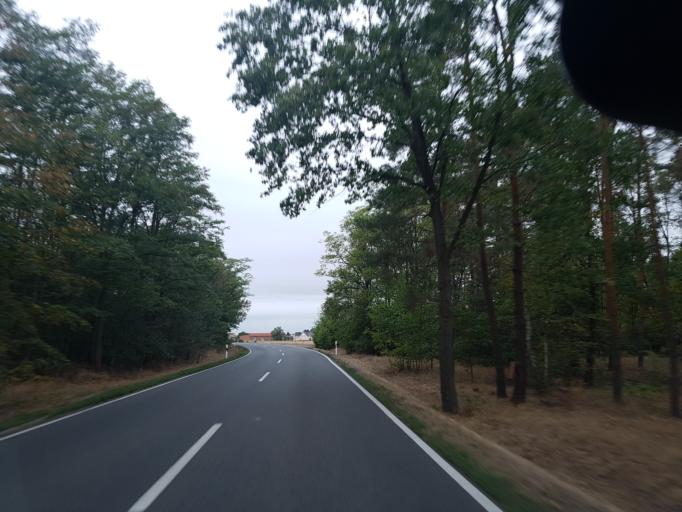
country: DE
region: Saxony-Anhalt
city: Prettin
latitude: 51.6548
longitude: 12.9505
